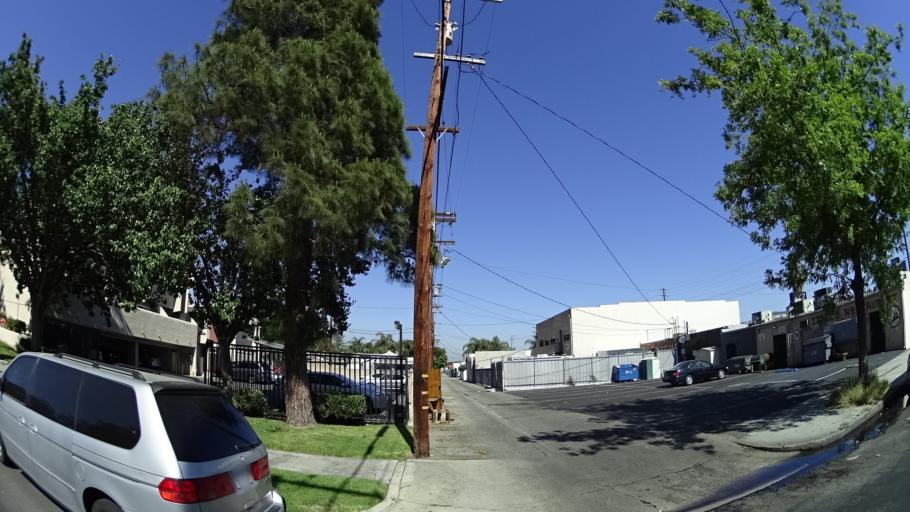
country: US
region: California
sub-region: Los Angeles County
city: North Hollywood
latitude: 34.1725
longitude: -118.3649
